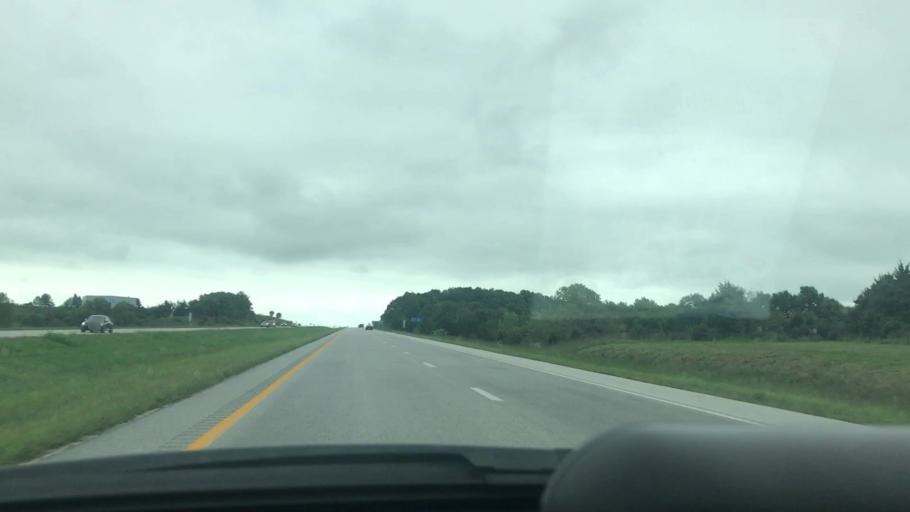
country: US
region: Missouri
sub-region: Greene County
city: Strafford
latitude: 37.2939
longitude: -93.1801
